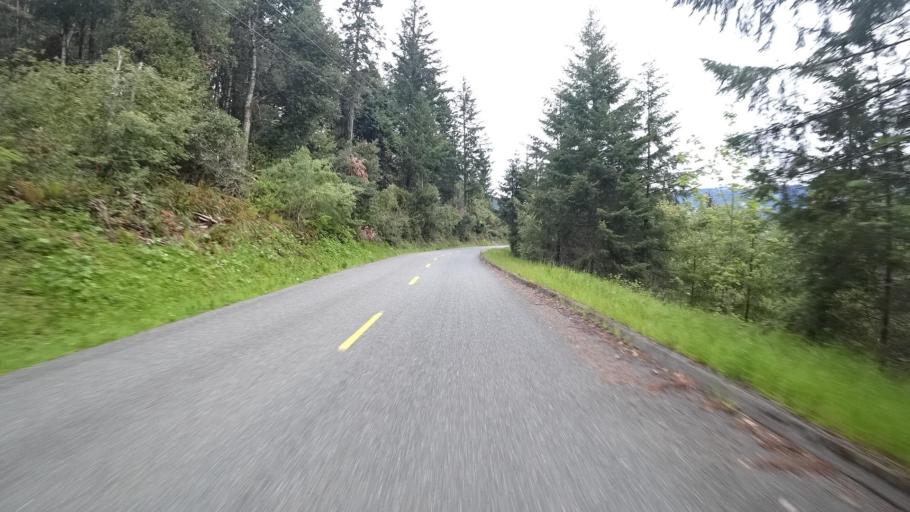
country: US
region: California
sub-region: Humboldt County
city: Blue Lake
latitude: 40.9310
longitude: -123.8451
